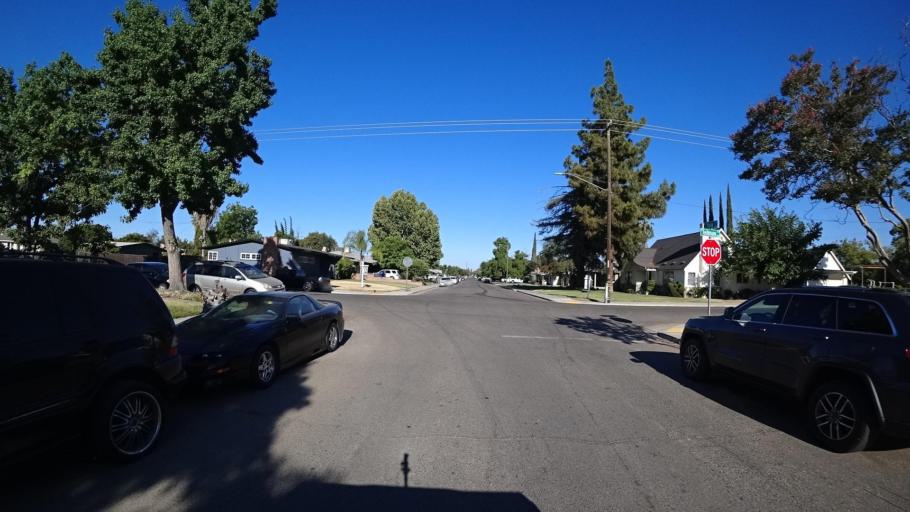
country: US
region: California
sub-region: Fresno County
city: Fresno
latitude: 36.7702
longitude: -119.8220
